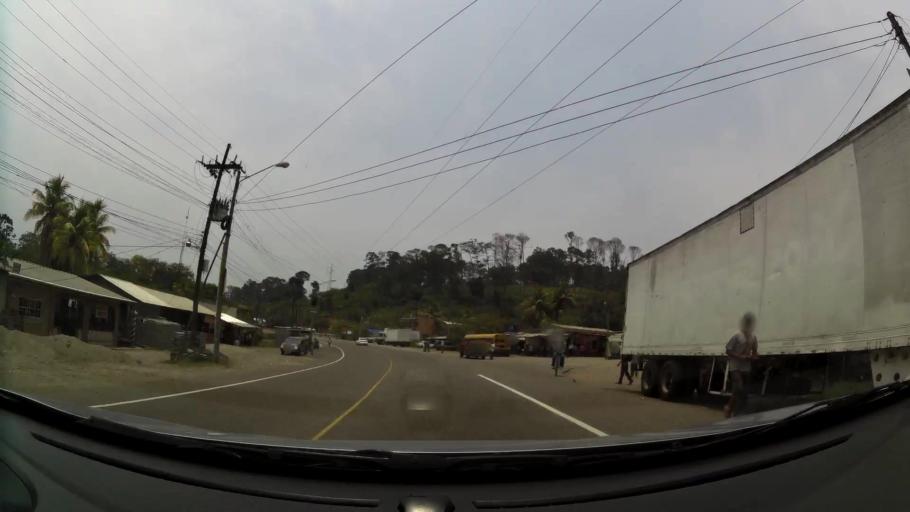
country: HN
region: Cortes
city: La Guama
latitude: 14.8890
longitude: -87.9385
